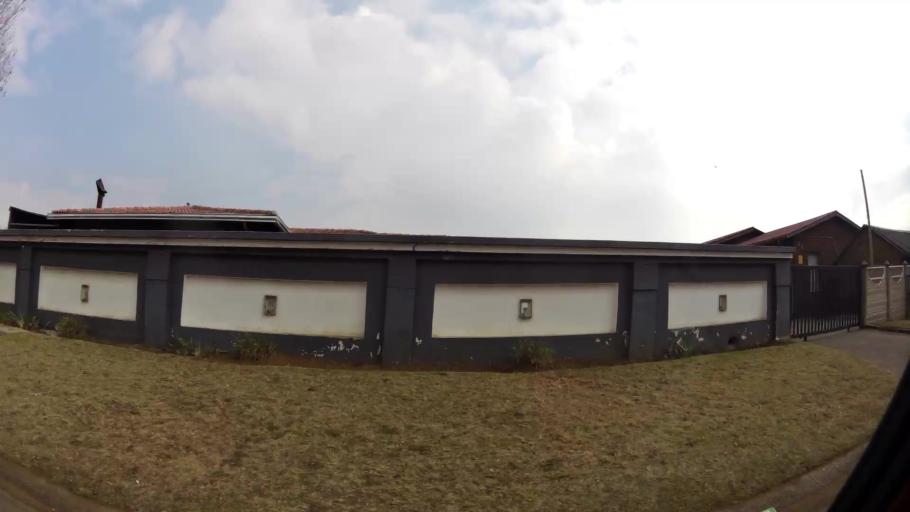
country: ZA
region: Gauteng
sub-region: Sedibeng District Municipality
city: Vanderbijlpark
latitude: -26.6810
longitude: 27.8358
